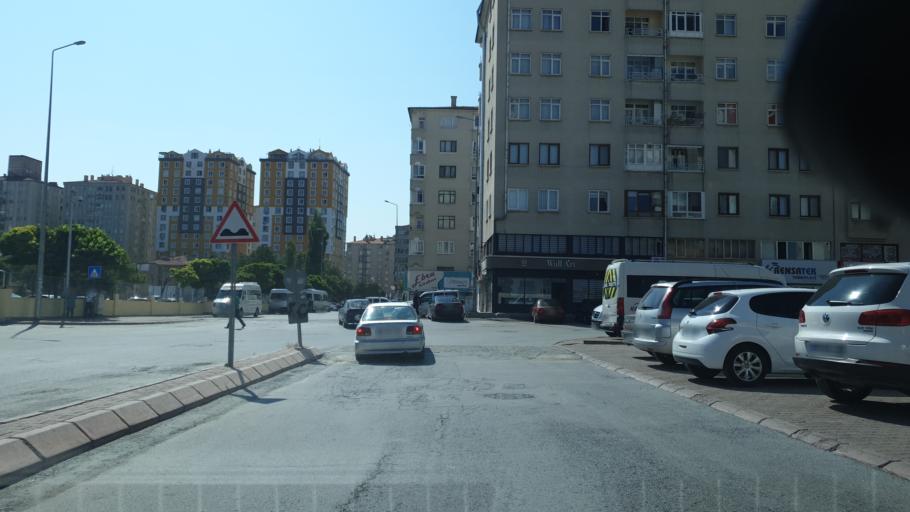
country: TR
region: Kayseri
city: Kayseri
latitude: 38.7265
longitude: 35.4912
